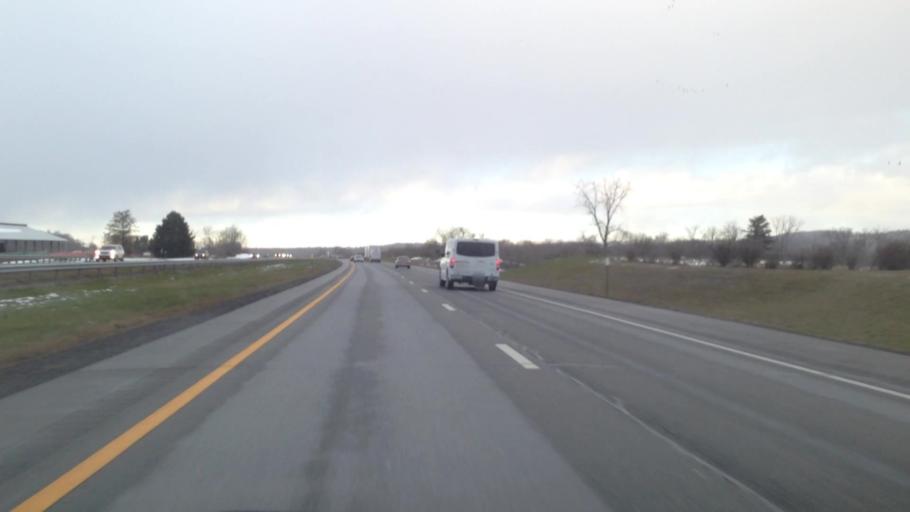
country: US
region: New York
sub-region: Montgomery County
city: Saint Johnsville
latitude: 42.9793
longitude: -74.6557
